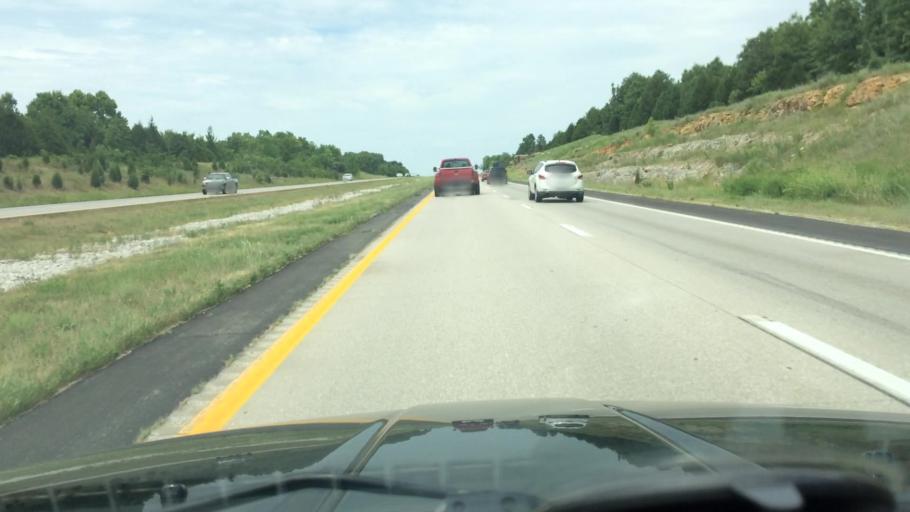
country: US
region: Missouri
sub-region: Greene County
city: Willard
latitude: 37.4388
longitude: -93.3555
